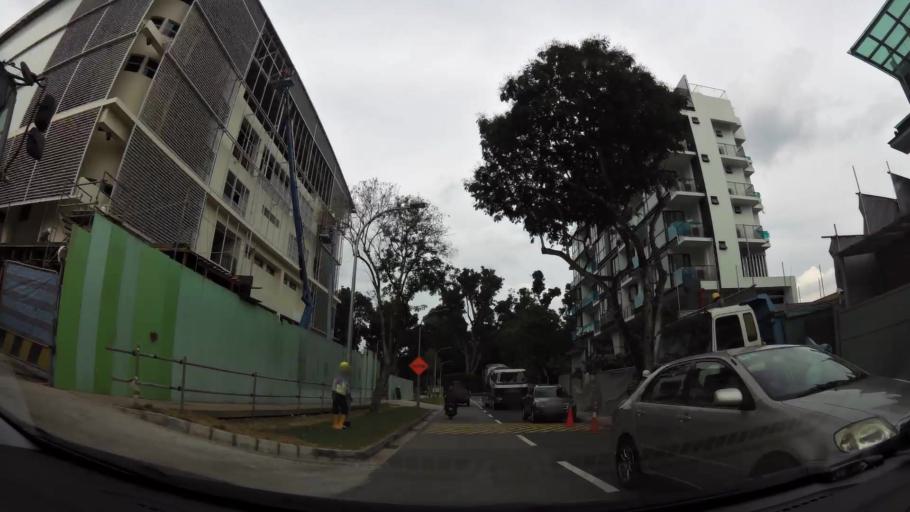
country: SG
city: Singapore
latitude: 1.3247
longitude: 103.8081
